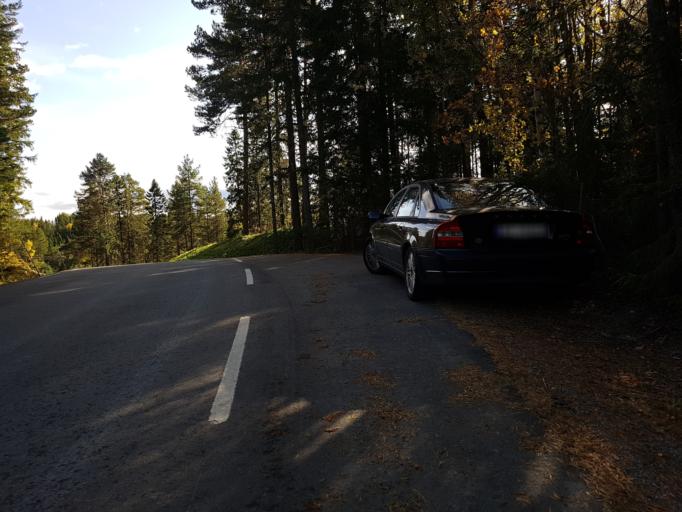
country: NO
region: Sor-Trondelag
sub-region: Malvik
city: Malvik
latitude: 63.3821
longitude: 10.5974
